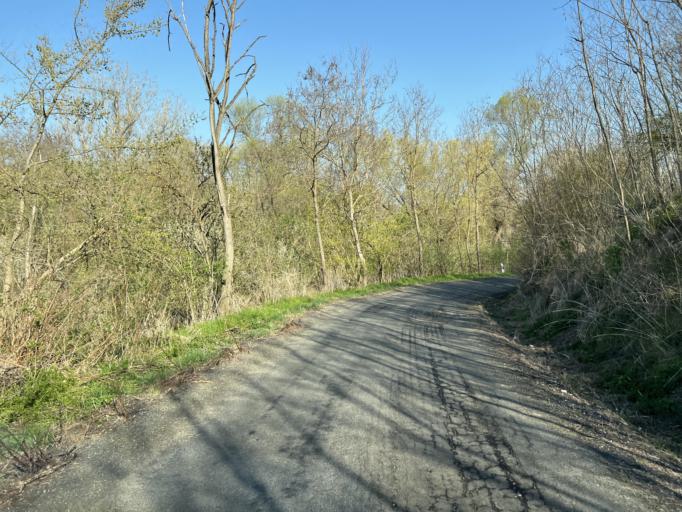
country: SK
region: Nitriansky
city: Sahy
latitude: 48.0048
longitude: 18.8211
